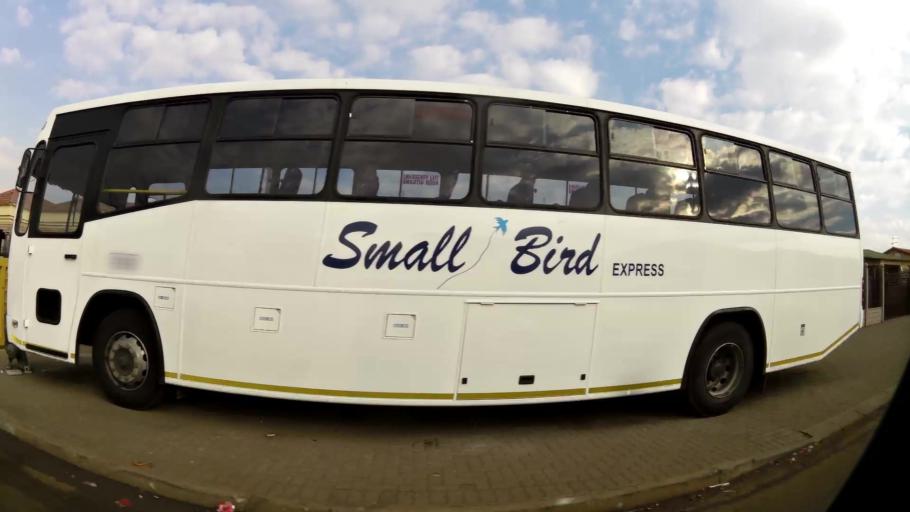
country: ZA
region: Gauteng
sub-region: Sedibeng District Municipality
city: Vanderbijlpark
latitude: -26.6976
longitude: 27.8704
